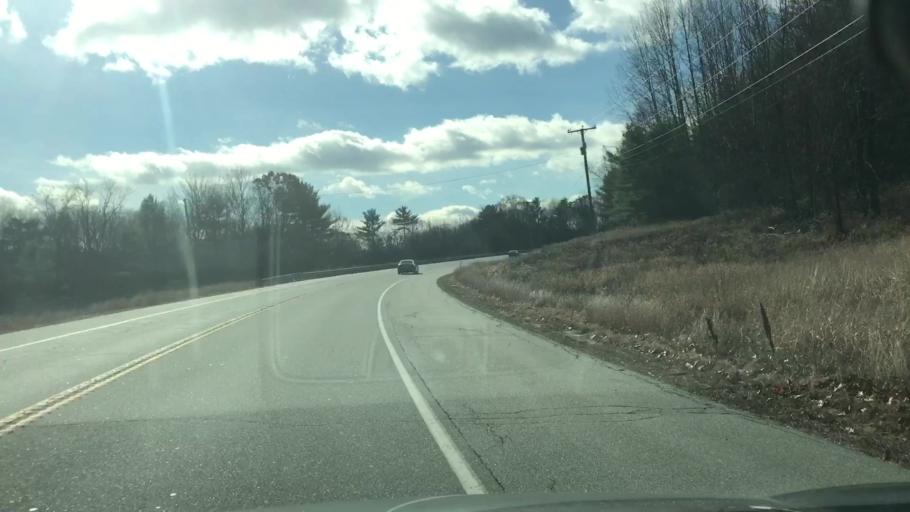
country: US
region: New Hampshire
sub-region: Belknap County
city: Barnstead
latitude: 43.3189
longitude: -71.3055
